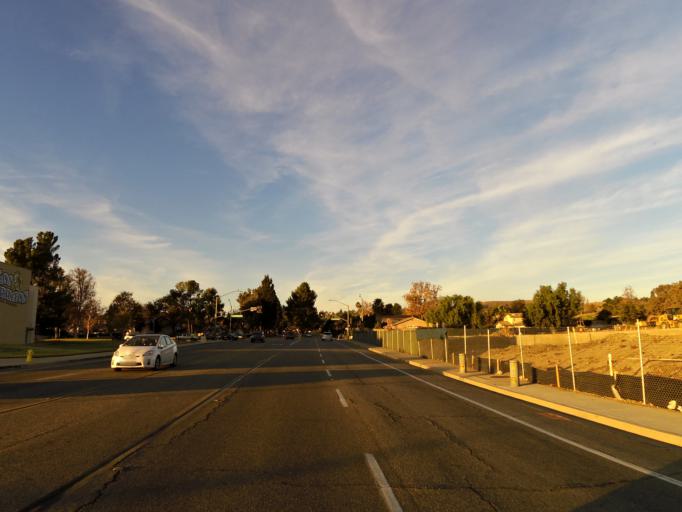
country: US
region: California
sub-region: Ventura County
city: Thousand Oaks
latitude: 34.2068
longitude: -118.8396
